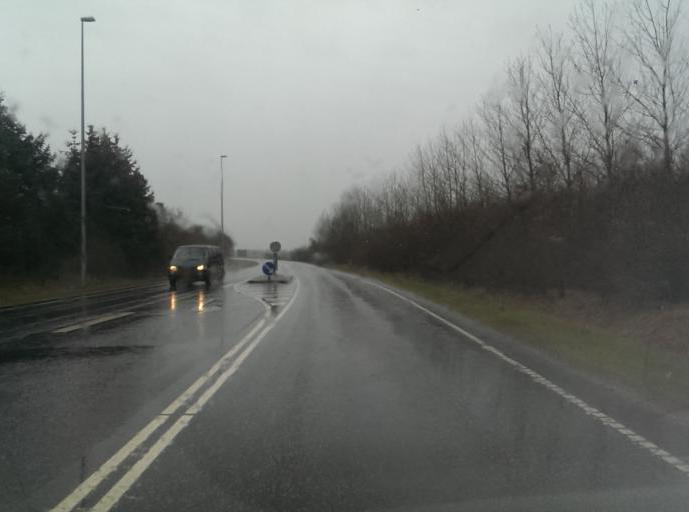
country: DK
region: Central Jutland
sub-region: Ringkobing-Skjern Kommune
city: Tarm
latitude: 55.9025
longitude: 8.5044
